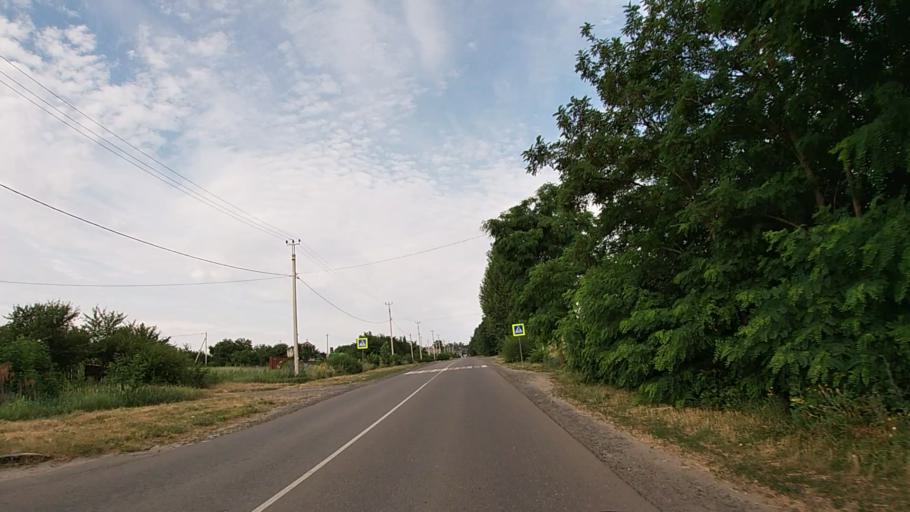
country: RU
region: Belgorod
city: Severnyy
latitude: 50.6924
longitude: 36.5652
